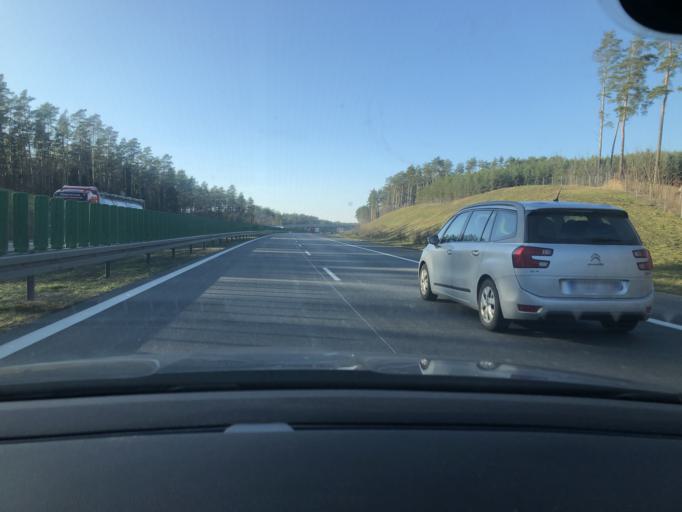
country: PL
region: Lubusz
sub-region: Powiat sulecinski
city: Torzym
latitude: 52.3248
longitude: 15.0636
